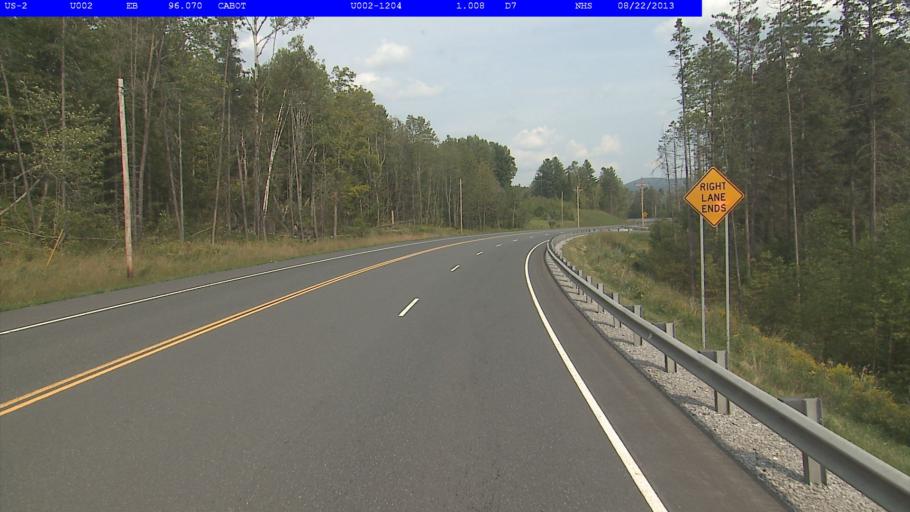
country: US
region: Vermont
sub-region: Caledonia County
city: Hardwick
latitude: 44.3637
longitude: -72.3050
